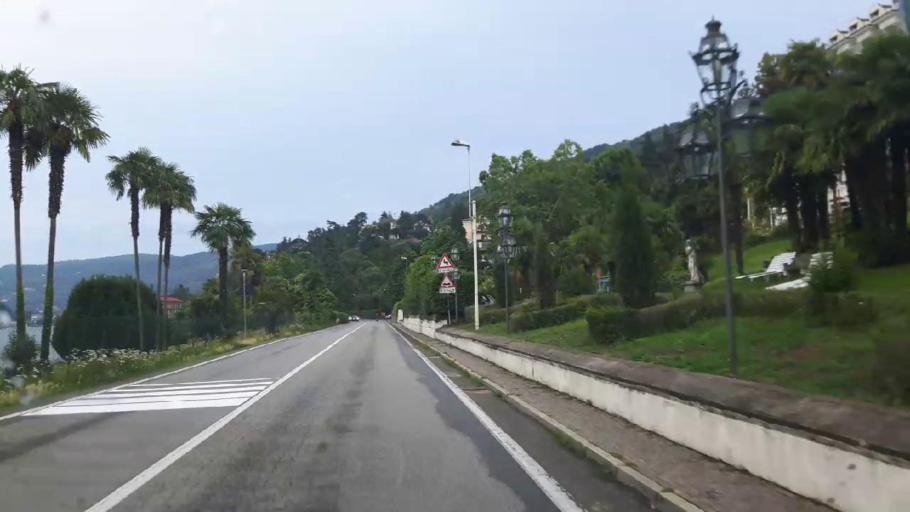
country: IT
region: Piedmont
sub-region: Provincia Verbano-Cusio-Ossola
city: Baveno
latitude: 45.9030
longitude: 8.5082
